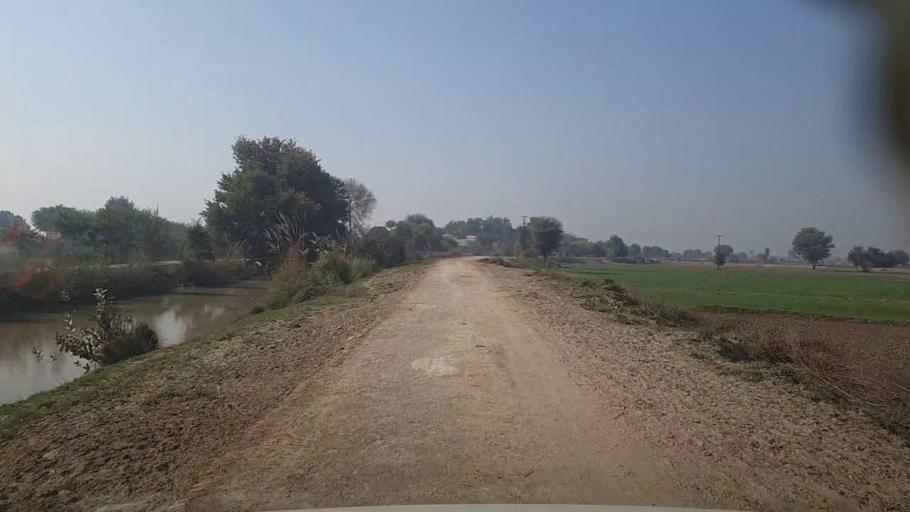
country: PK
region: Sindh
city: Kandiari
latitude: 27.0022
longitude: 68.4897
